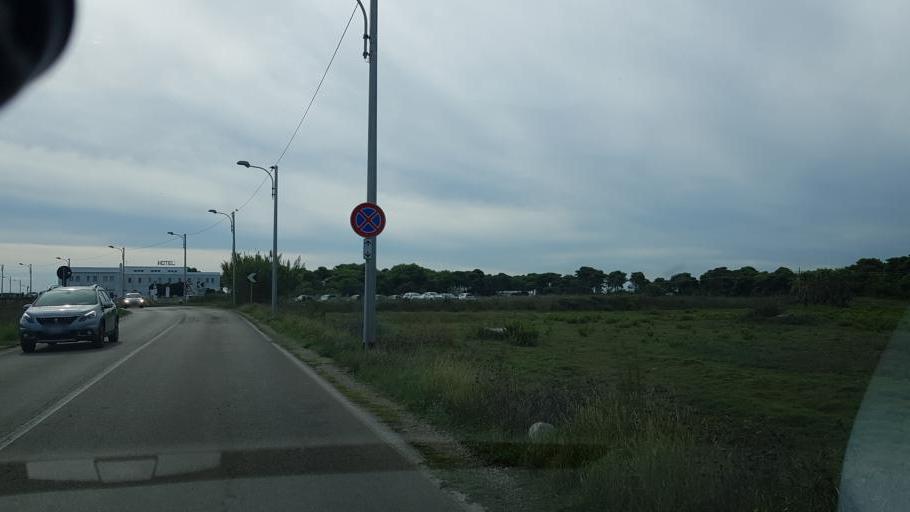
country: IT
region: Apulia
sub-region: Provincia di Lecce
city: Borgagne
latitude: 40.2883
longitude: 18.4243
